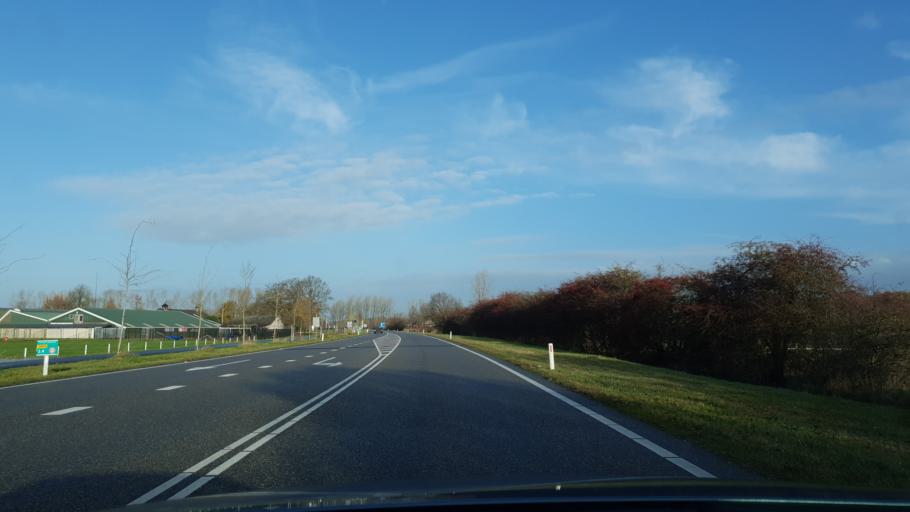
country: NL
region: Gelderland
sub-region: Gemeente Wijchen
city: Wijchen
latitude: 51.8150
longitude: 5.6924
